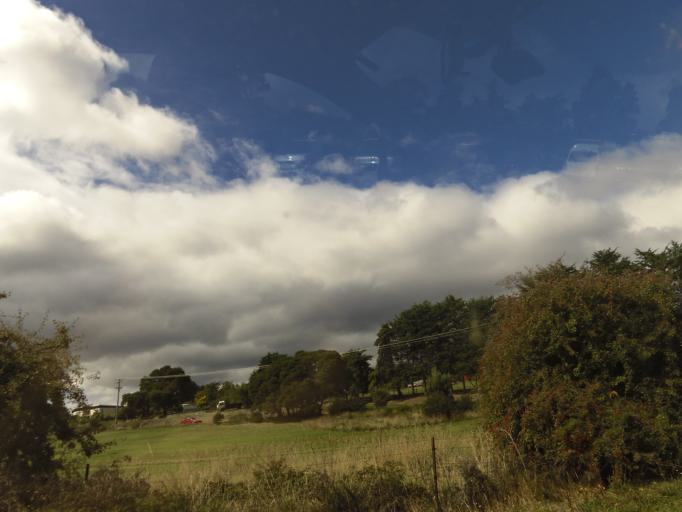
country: AU
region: Tasmania
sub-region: Huon Valley
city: Huonville
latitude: -43.0060
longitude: 147.0421
